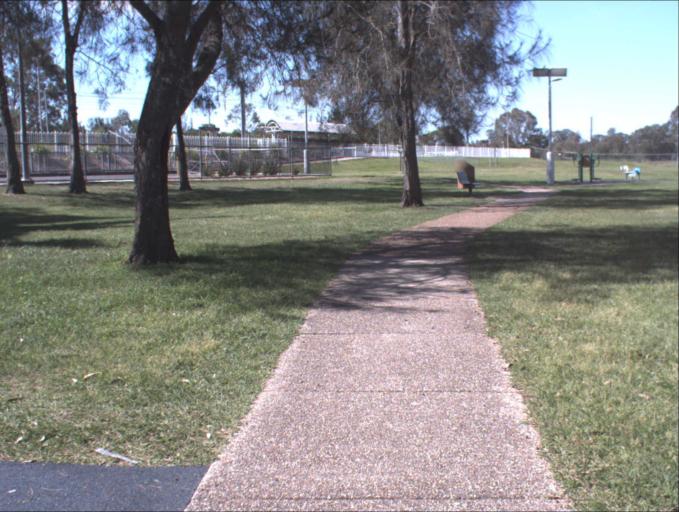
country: AU
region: Queensland
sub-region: Logan
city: Beenleigh
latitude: -27.6987
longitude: 153.1706
